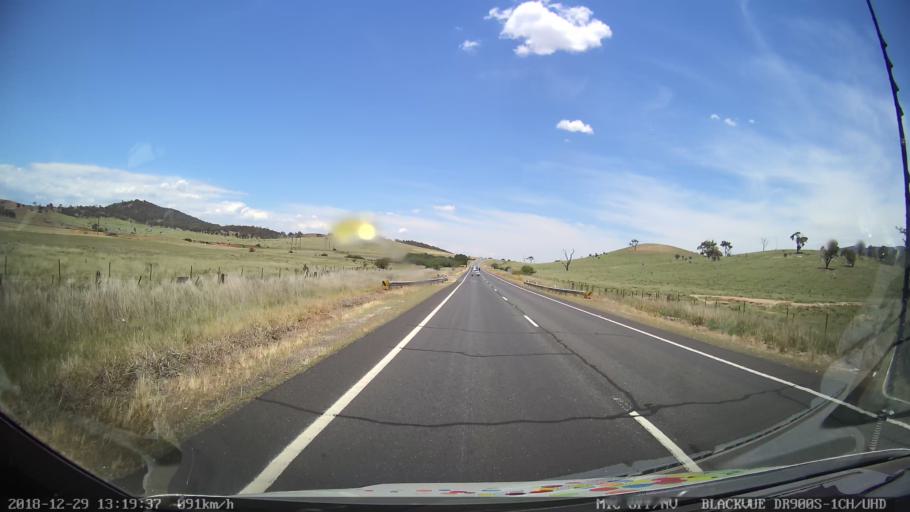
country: AU
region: Australian Capital Territory
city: Macarthur
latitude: -35.7680
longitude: 149.1613
